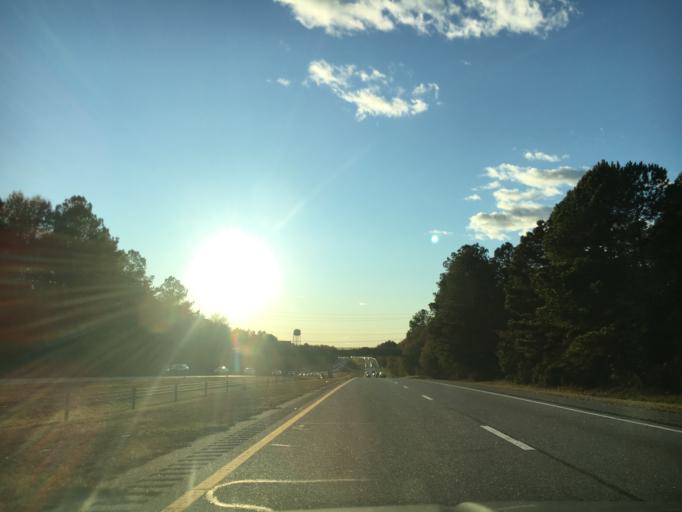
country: US
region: South Carolina
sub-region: Richland County
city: Forest Acres
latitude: 34.0503
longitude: -80.9997
